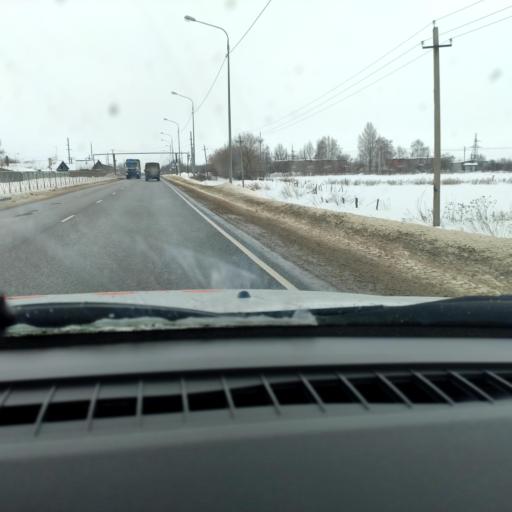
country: RU
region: Samara
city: Dubovyy Umet
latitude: 52.9626
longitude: 50.2894
